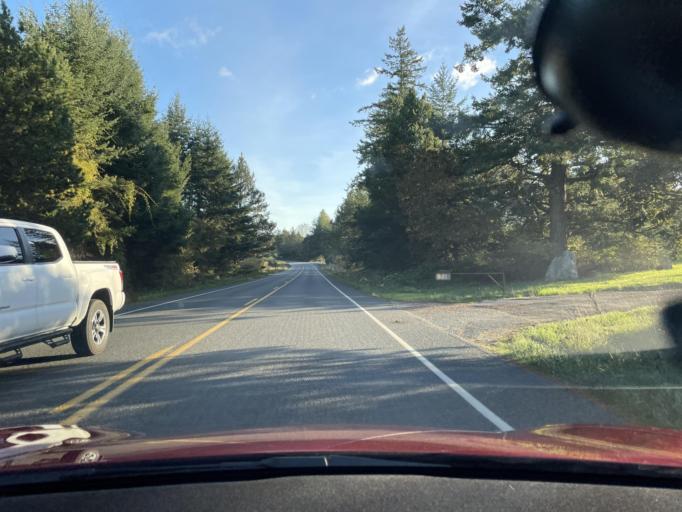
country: US
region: Washington
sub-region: San Juan County
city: Friday Harbor
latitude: 48.5055
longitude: -123.0362
